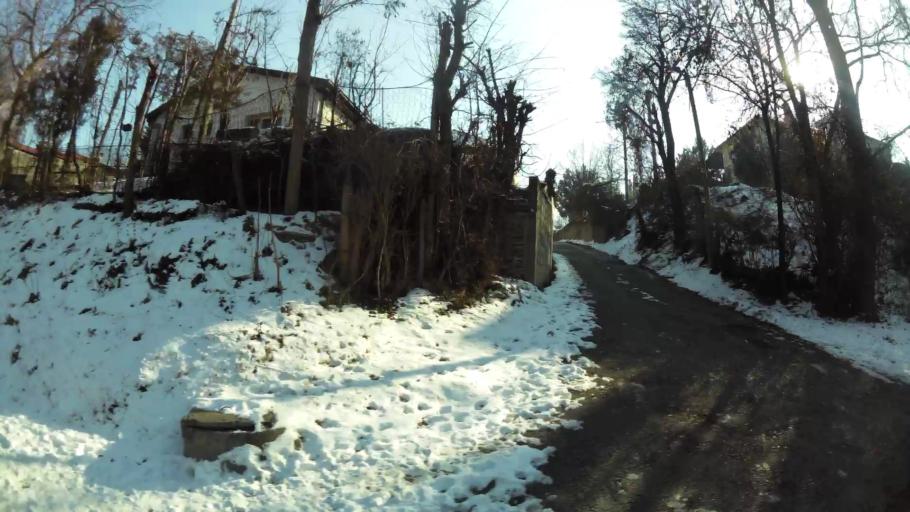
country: MK
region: Kisela Voda
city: Usje
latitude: 41.9662
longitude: 21.4466
